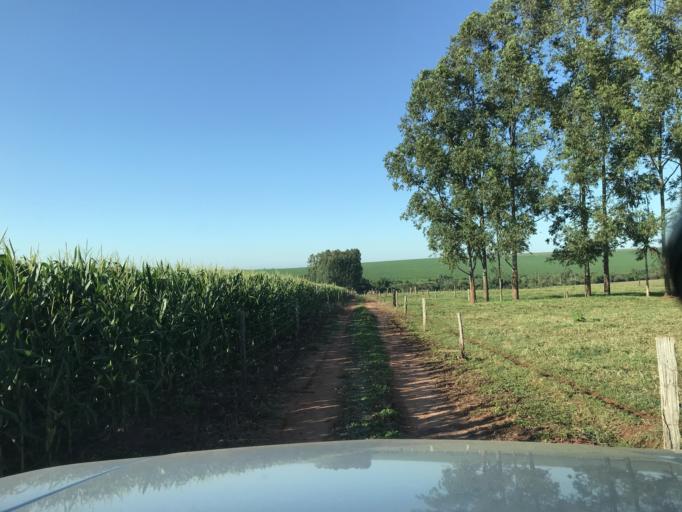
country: BR
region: Parana
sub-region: Palotina
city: Palotina
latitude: -24.2147
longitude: -53.7583
